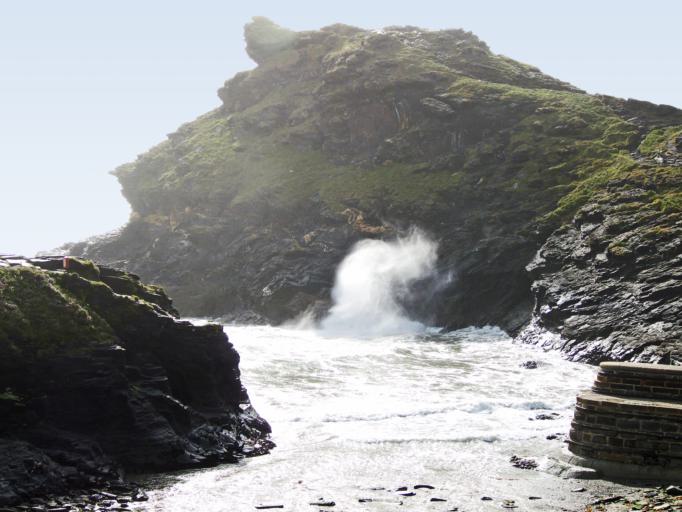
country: GB
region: England
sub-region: Cornwall
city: Tintagel
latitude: 50.6921
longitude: -4.6976
